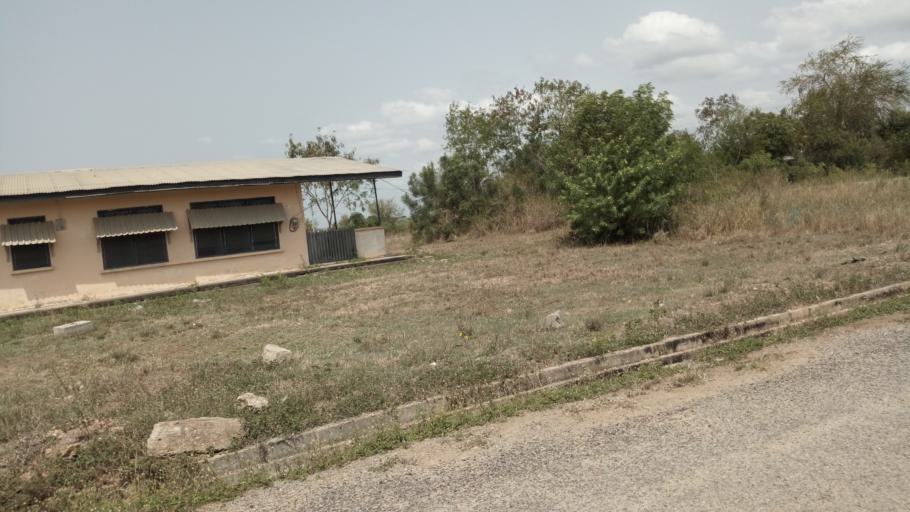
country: GH
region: Central
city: Winneba
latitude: 5.3671
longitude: -0.6450
